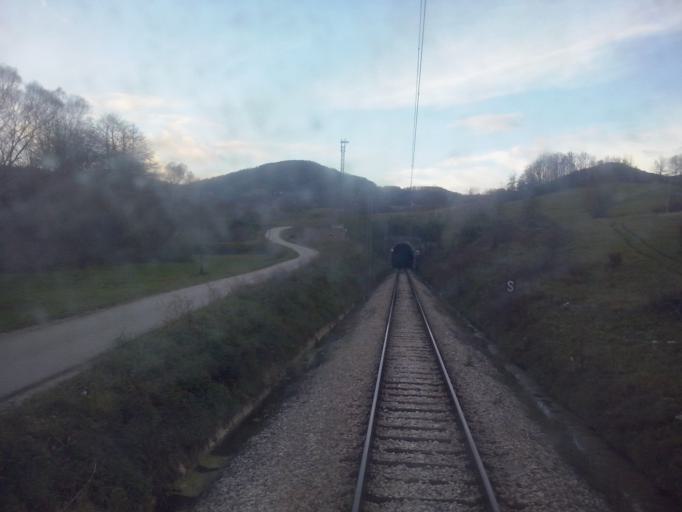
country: RS
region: Central Serbia
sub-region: Zlatiborski Okrug
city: Kosjeric
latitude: 44.0885
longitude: 19.8856
